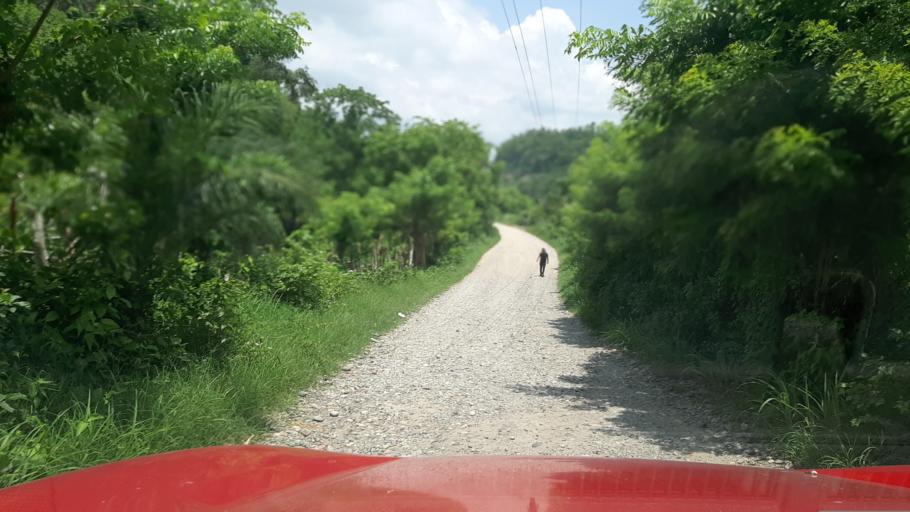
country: MX
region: Veracruz
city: Papantla de Olarte
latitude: 20.4390
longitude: -97.2787
